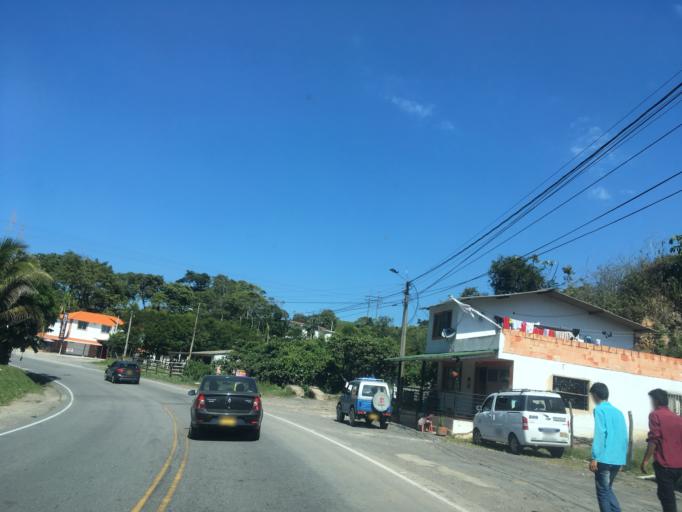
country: CO
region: Santander
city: Suaita
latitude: 6.0718
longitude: -73.4084
